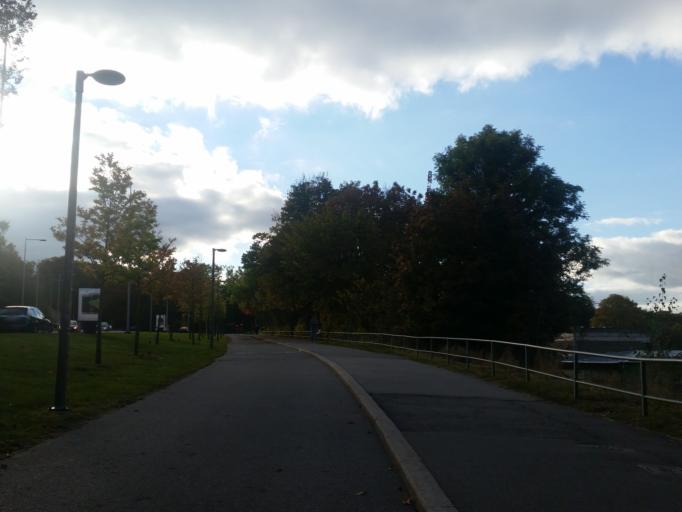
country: SE
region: Stockholm
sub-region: Stockholms Kommun
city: Arsta
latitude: 59.3005
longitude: 18.0887
